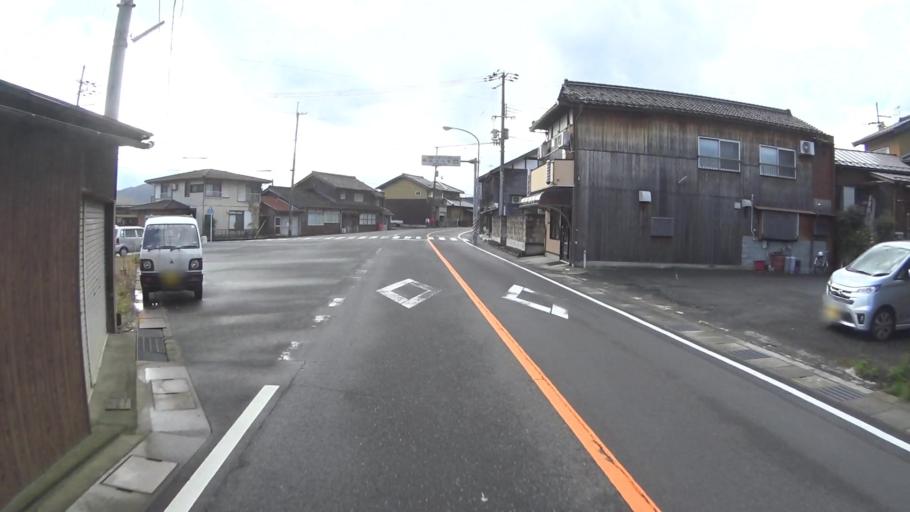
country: JP
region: Kyoto
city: Miyazu
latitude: 35.5442
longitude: 135.1259
